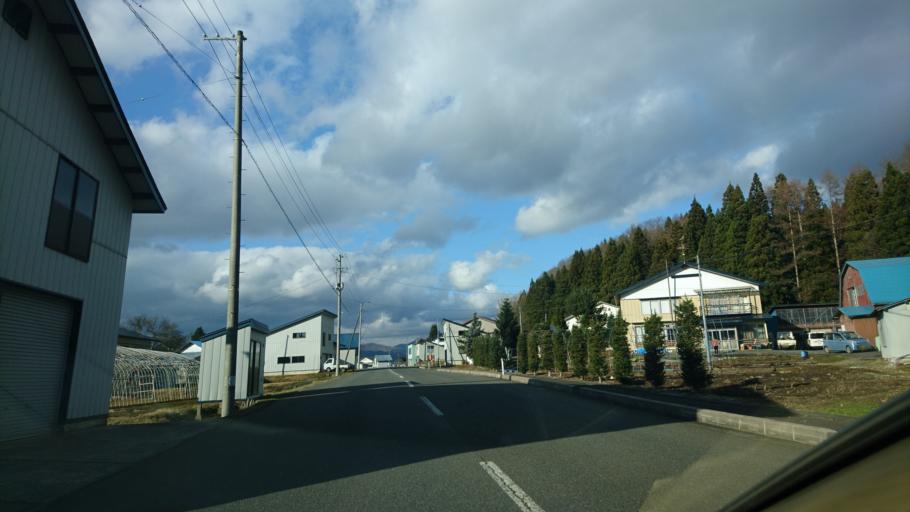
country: JP
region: Akita
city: Yokotemachi
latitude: 39.3736
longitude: 140.7692
